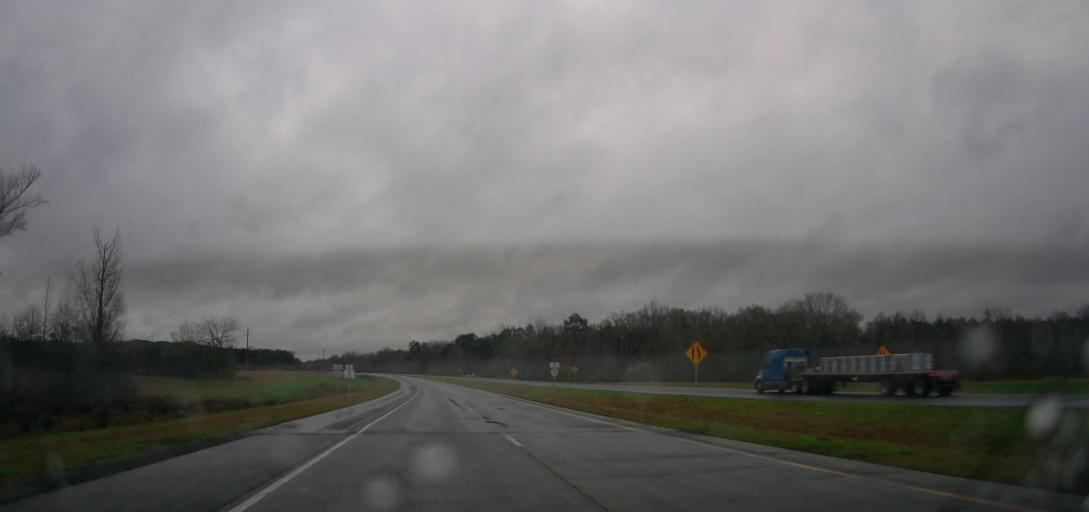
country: US
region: Alabama
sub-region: Bibb County
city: Centreville
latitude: 32.9355
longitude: -87.0628
